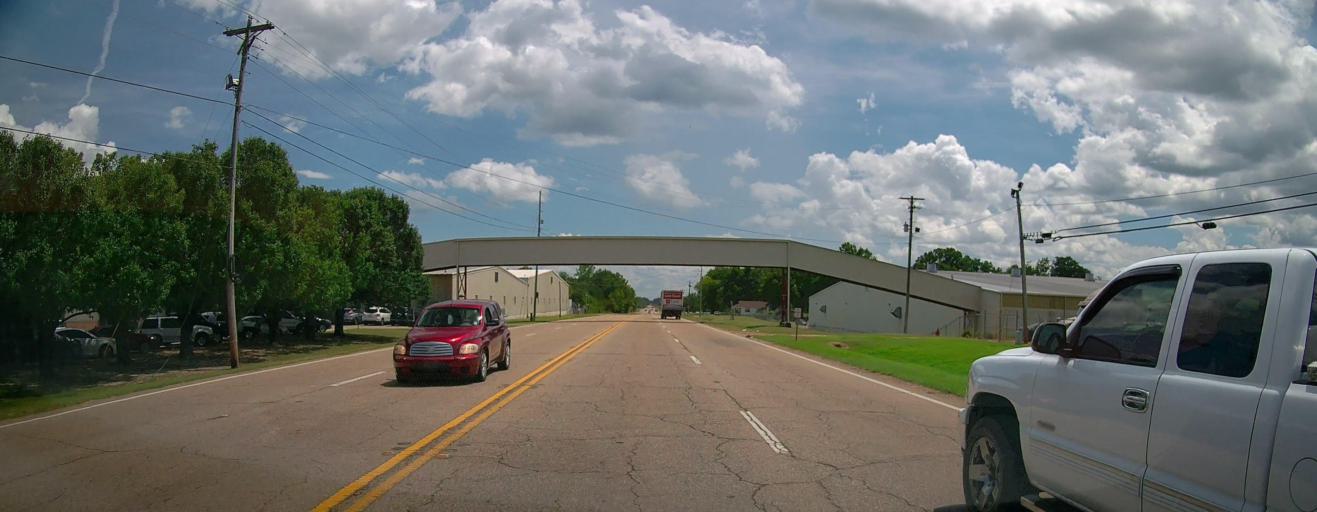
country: US
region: Mississippi
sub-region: Lee County
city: Verona
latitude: 34.1613
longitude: -88.7195
